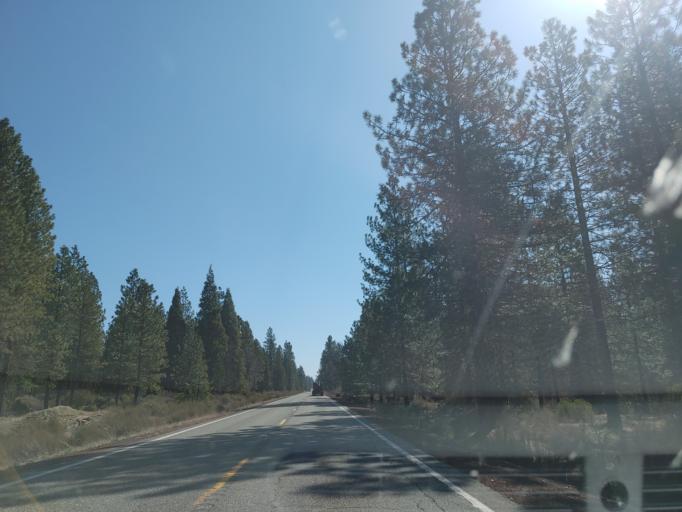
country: US
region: California
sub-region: Siskiyou County
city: McCloud
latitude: 41.2532
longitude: -122.0913
